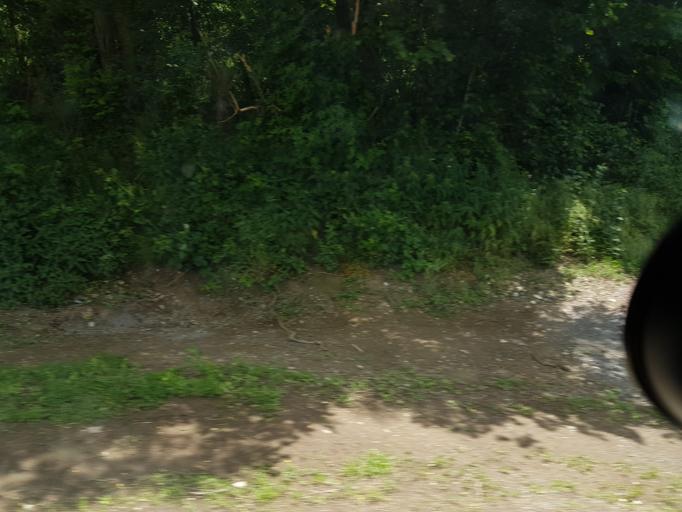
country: FR
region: Bourgogne
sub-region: Departement de la Cote-d'Or
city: Saulieu
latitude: 47.1265
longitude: 4.2201
